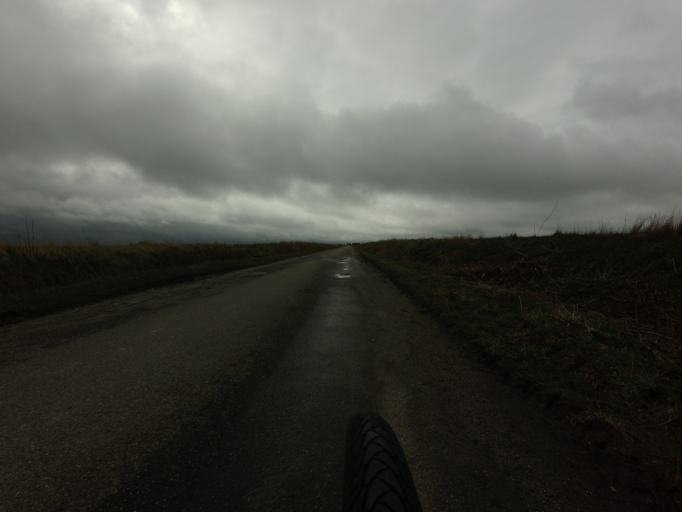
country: DK
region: North Denmark
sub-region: Hjorring Kommune
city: Vra
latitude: 57.3764
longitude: 9.8388
